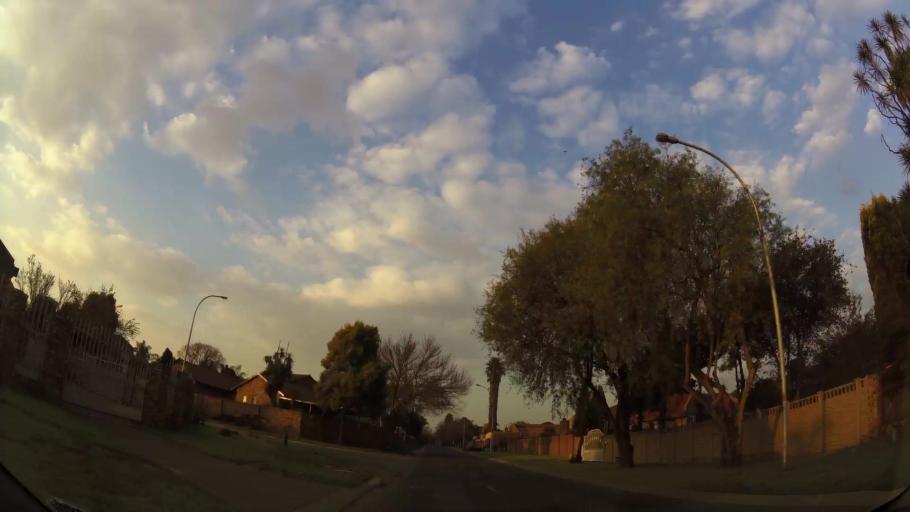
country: ZA
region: Gauteng
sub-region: Ekurhuleni Metropolitan Municipality
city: Benoni
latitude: -26.1670
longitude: 28.3047
